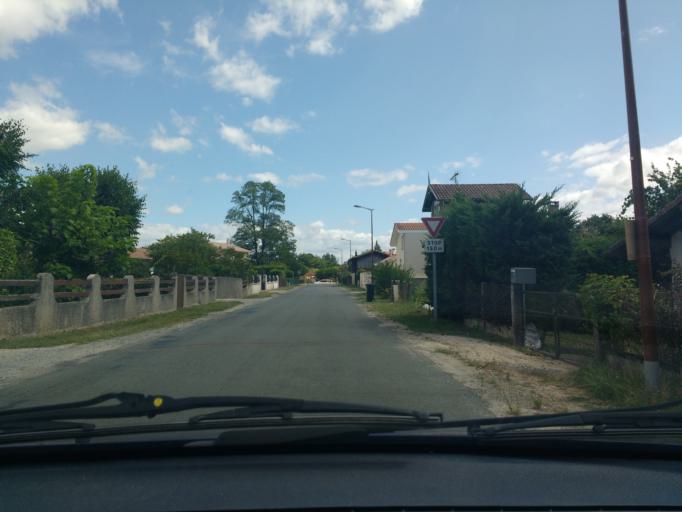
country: FR
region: Aquitaine
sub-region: Departement de la Gironde
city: Salles
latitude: 44.5495
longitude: -0.8650
